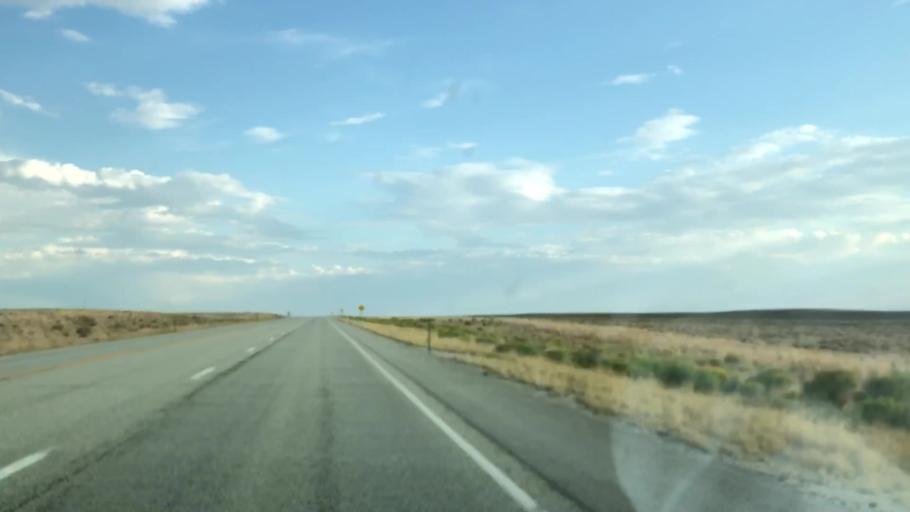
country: US
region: Wyoming
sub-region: Sweetwater County
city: North Rock Springs
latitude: 42.2681
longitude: -109.4771
